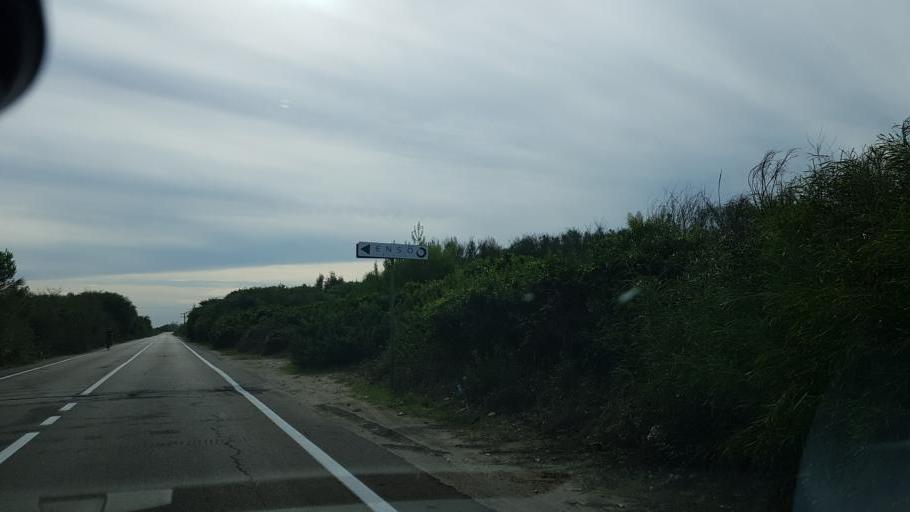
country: IT
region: Apulia
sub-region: Provincia di Lecce
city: Melendugno
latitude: 40.3102
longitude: 18.3919
